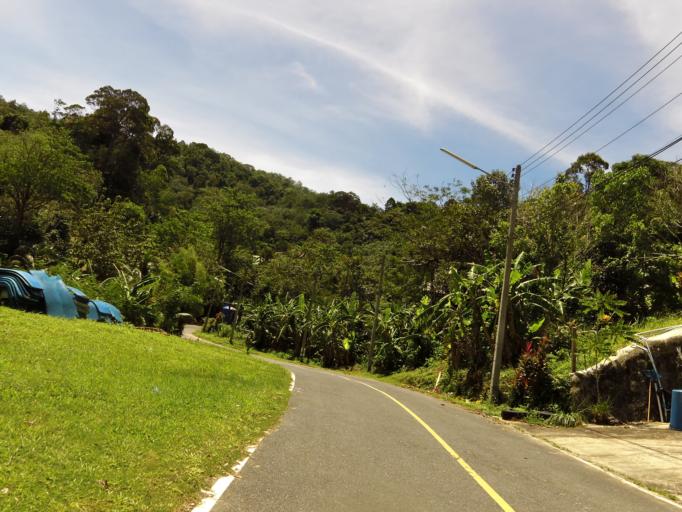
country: TH
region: Phuket
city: Ban Karon
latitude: 7.8460
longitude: 98.3090
